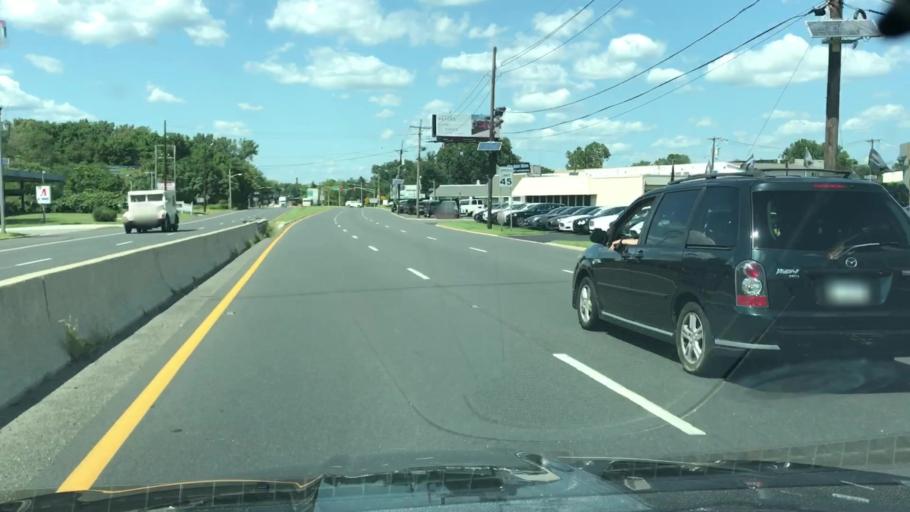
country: US
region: New Jersey
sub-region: Burlington County
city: Palmyra
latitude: 40.0022
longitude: -75.0367
